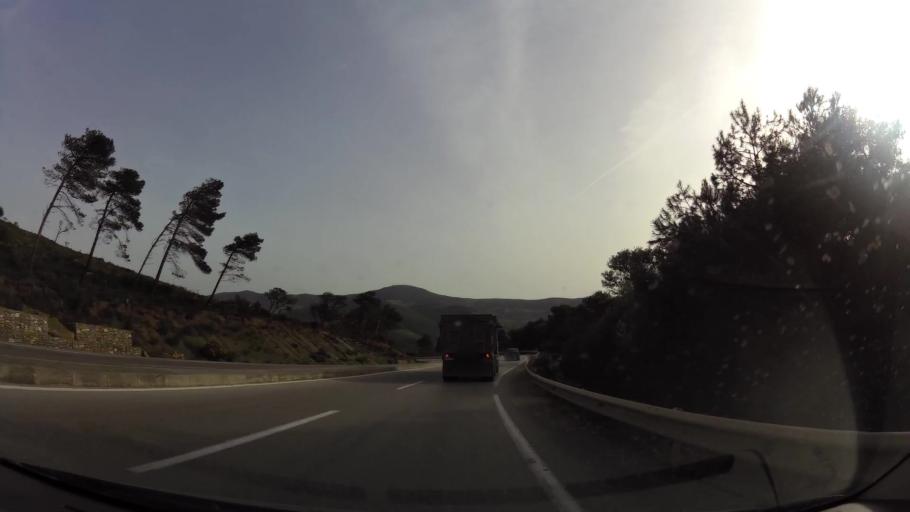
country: MA
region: Tanger-Tetouan
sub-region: Tetouan
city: Saddina
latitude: 35.5554
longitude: -5.5686
